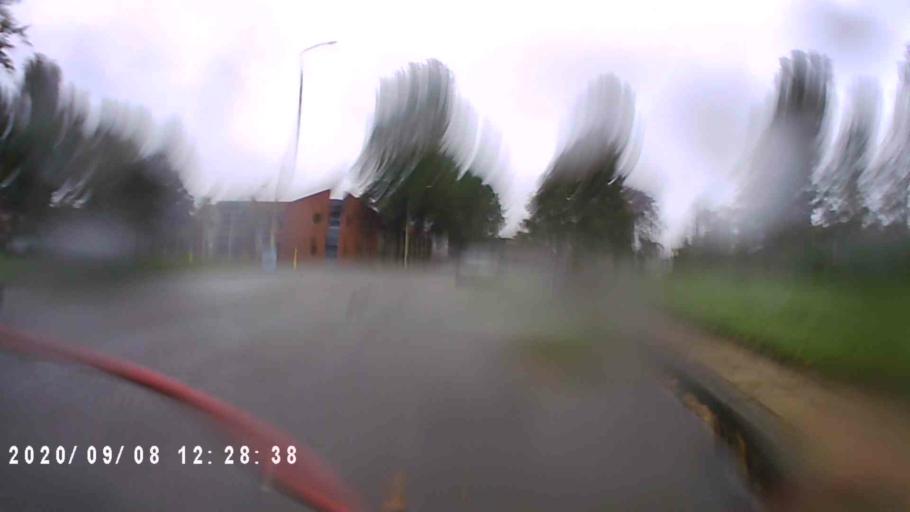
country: NL
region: Groningen
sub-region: Gemeente Veendam
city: Veendam
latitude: 53.1042
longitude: 6.8721
